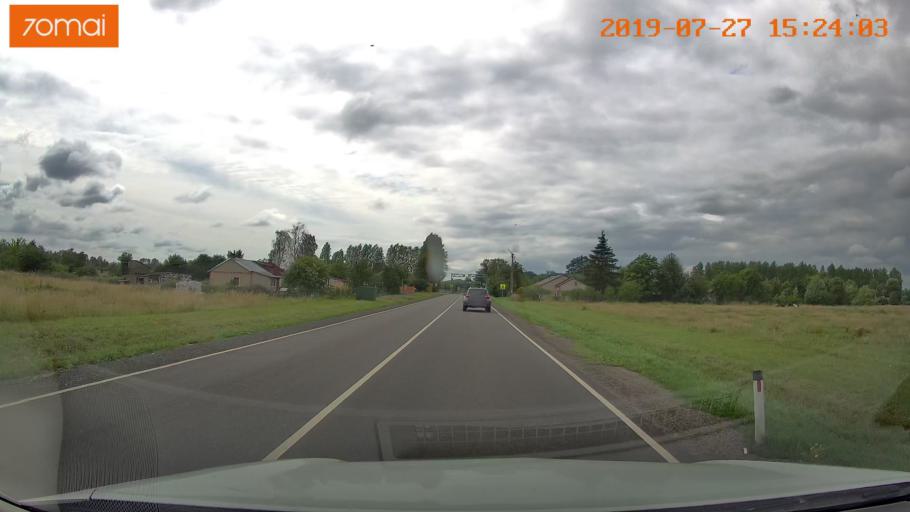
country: RU
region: Kaliningrad
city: Nesterov
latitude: 54.6361
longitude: 22.6176
